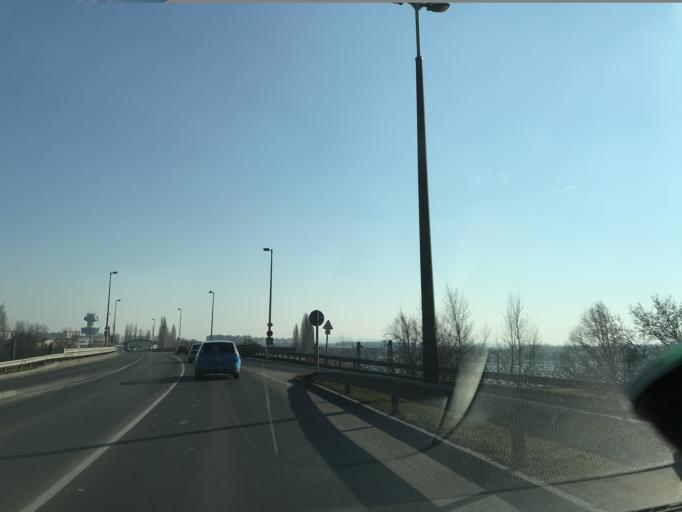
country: HU
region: Gyor-Moson-Sopron
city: Gyor
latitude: 47.6795
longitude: 17.6246
